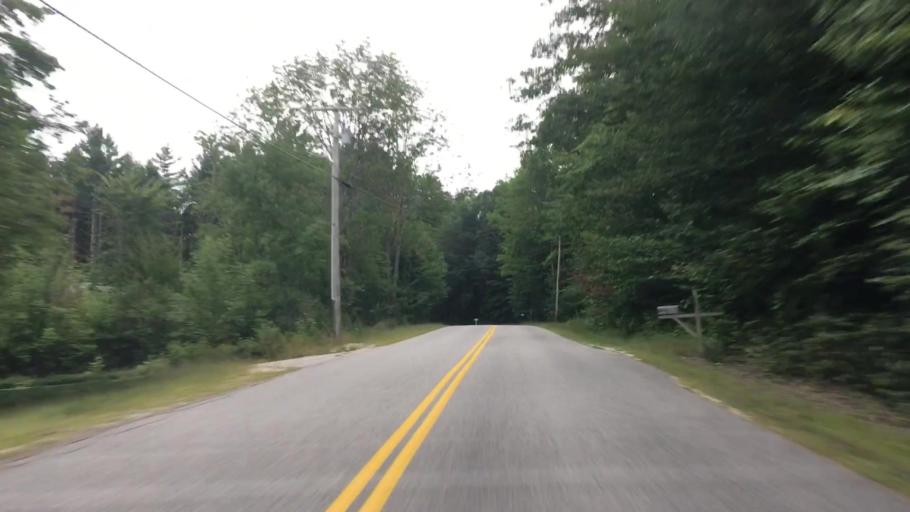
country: US
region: Maine
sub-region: Cumberland County
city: New Gloucester
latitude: 43.9194
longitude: -70.2542
